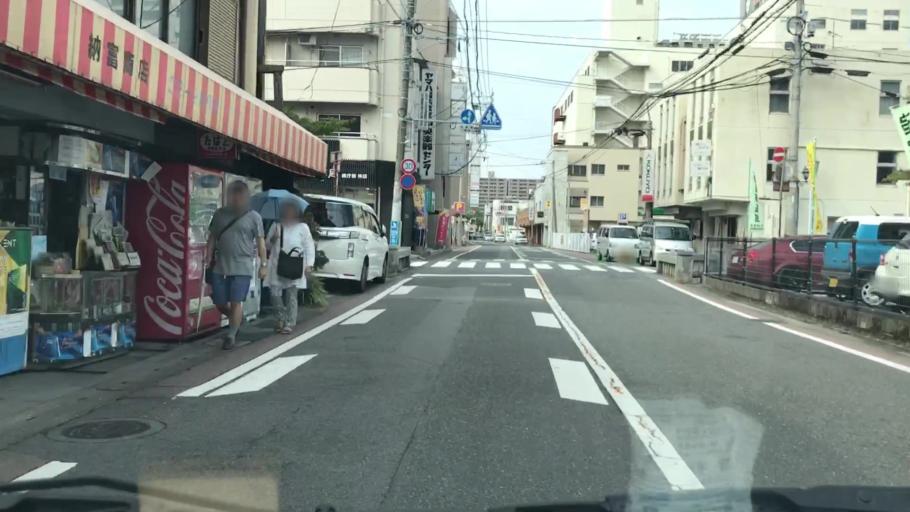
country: JP
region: Saga Prefecture
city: Saga-shi
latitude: 33.2513
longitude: 130.2993
